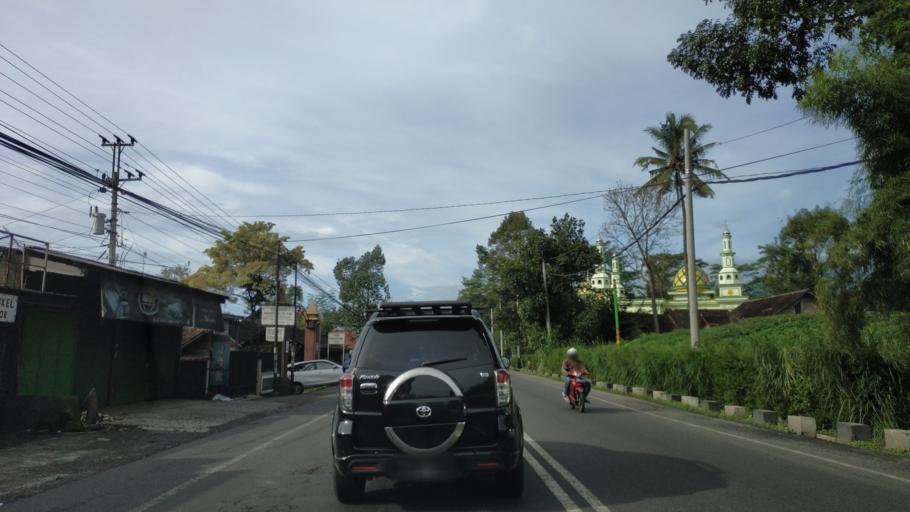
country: ID
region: Central Java
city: Salatiga
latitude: -7.3764
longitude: 110.5151
